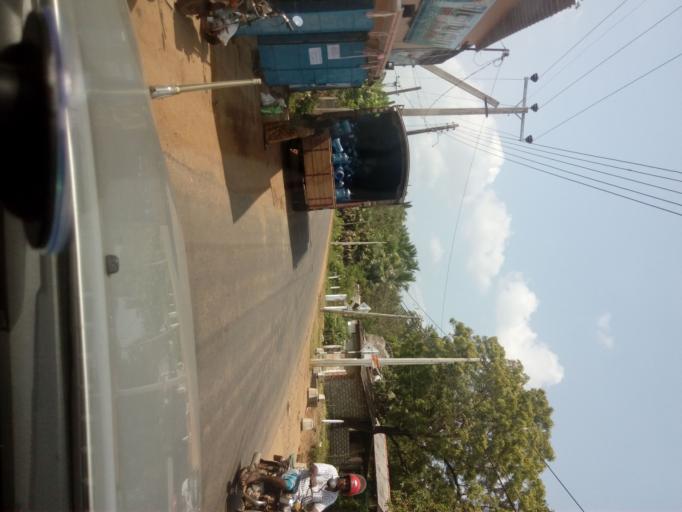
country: LK
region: Northern Province
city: Vavuniya
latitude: 8.7807
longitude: 80.4844
